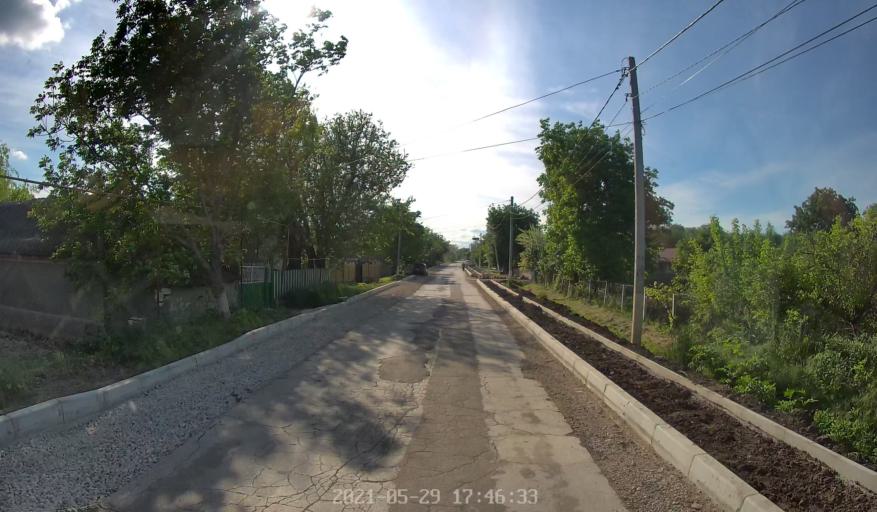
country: MD
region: Laloveni
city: Ialoveni
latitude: 46.8395
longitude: 28.8394
